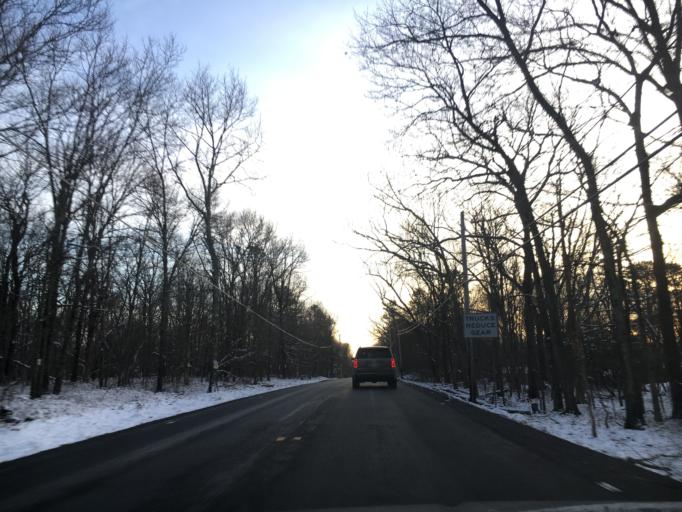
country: US
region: Pennsylvania
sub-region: Pike County
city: Saw Creek
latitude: 41.1304
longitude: -75.0879
